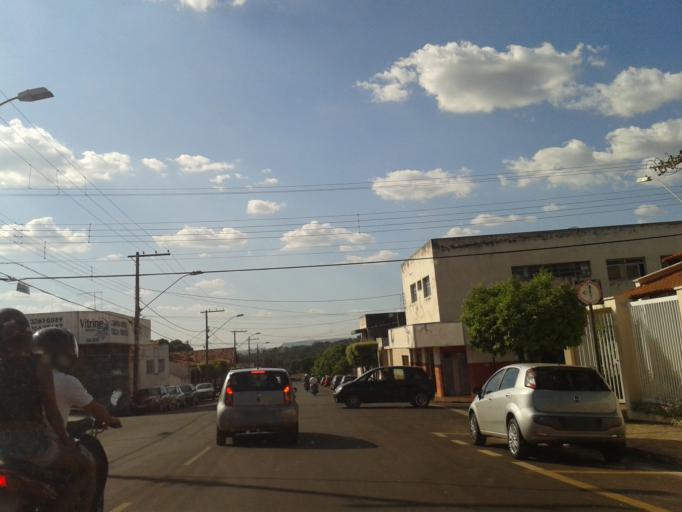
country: BR
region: Minas Gerais
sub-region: Ituiutaba
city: Ituiutaba
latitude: -18.9718
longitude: -49.4597
